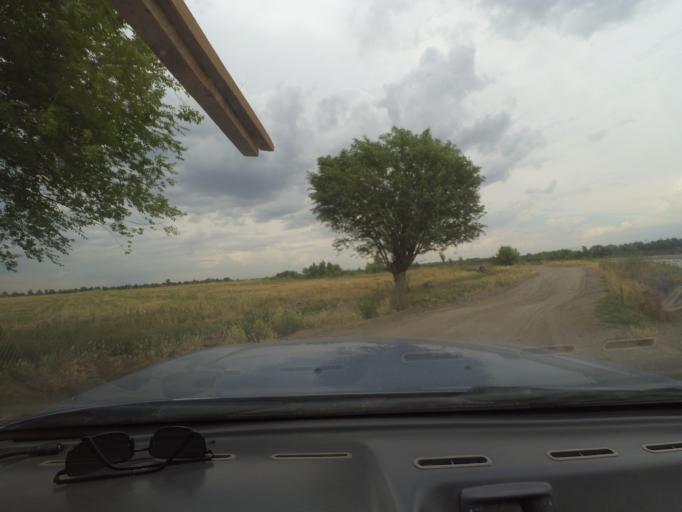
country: TJ
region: Viloyati Sughd
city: Buston
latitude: 40.5406
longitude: 69.0787
